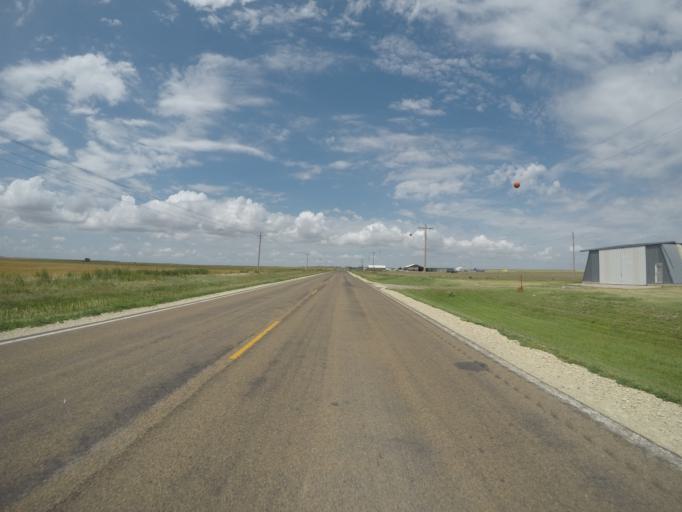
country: US
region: Kansas
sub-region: Rawlins County
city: Atwood
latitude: 39.8335
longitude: -101.0468
